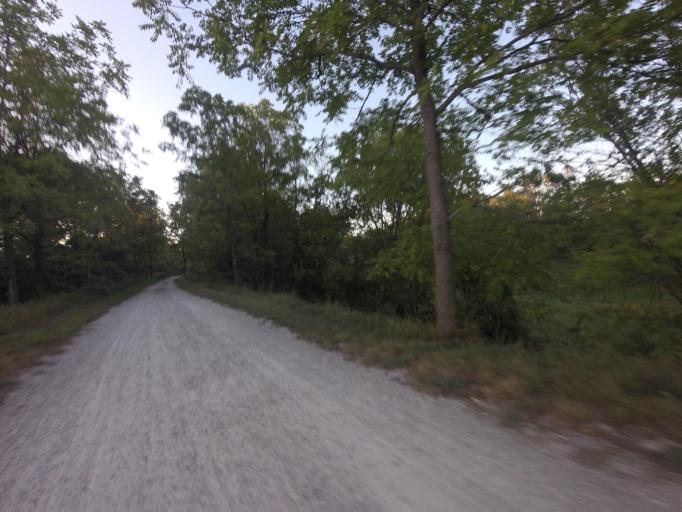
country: CA
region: Ontario
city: Brampton
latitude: 43.9131
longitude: -79.8400
